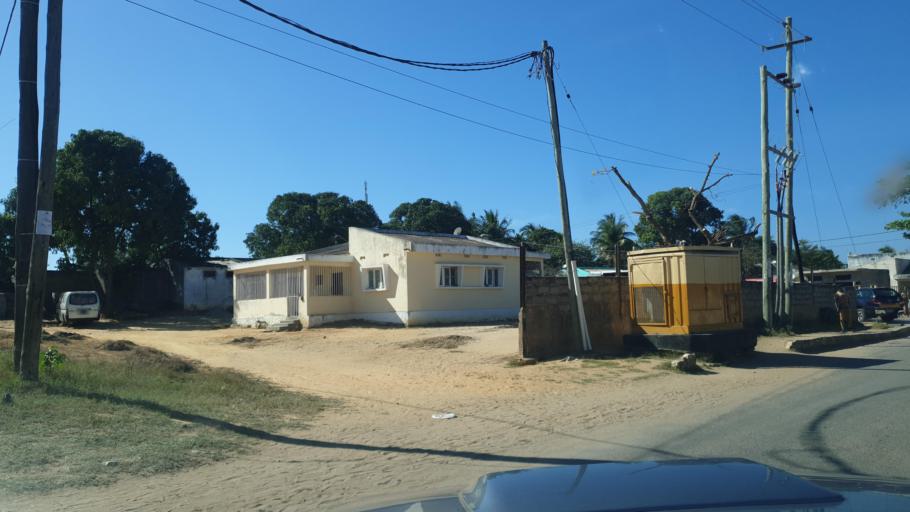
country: MZ
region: Nampula
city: Nacala
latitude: -14.5383
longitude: 40.6822
